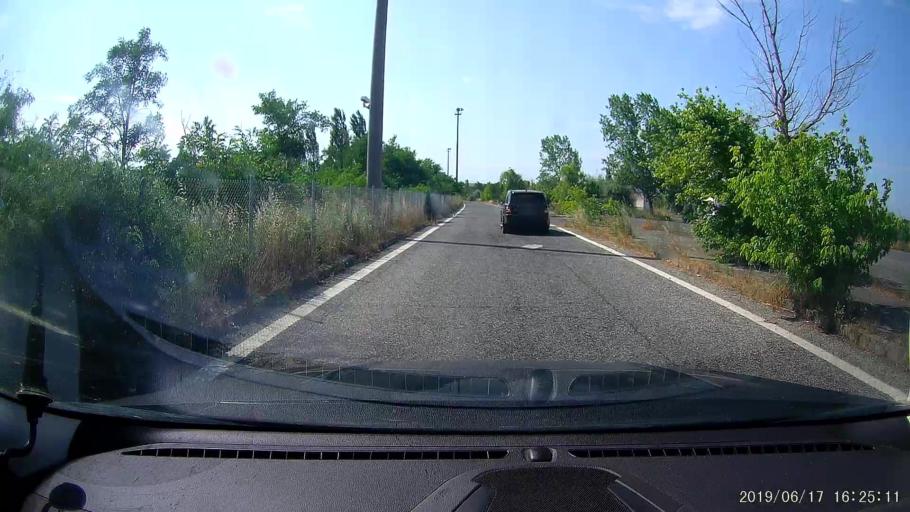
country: TR
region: Tekirdag
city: Marmaracik
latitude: 41.2904
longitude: 27.7829
